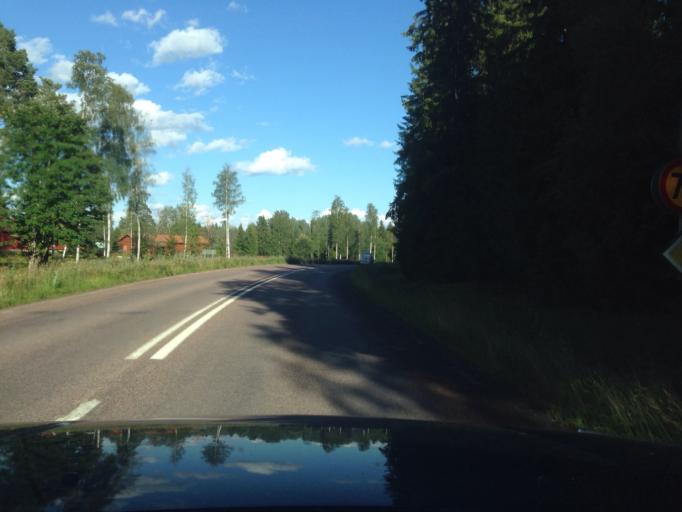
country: SE
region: Dalarna
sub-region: Ludvika Kommun
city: Ludvika
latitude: 60.1474
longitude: 15.0991
